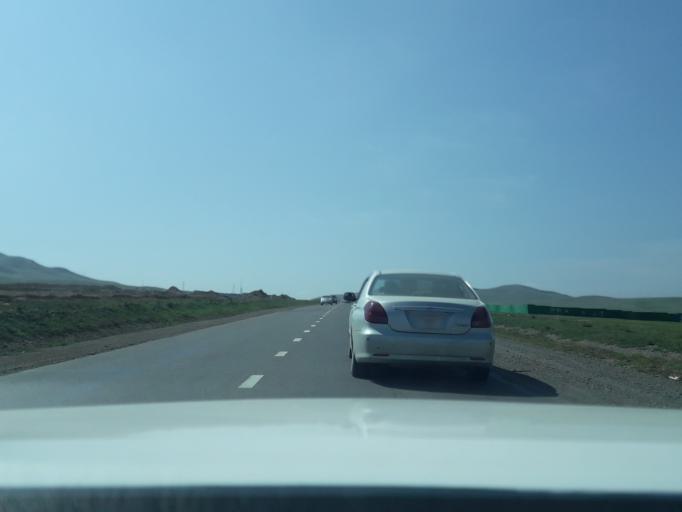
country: MN
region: Ulaanbaatar
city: Ulaanbaatar
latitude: 47.8140
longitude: 106.7547
